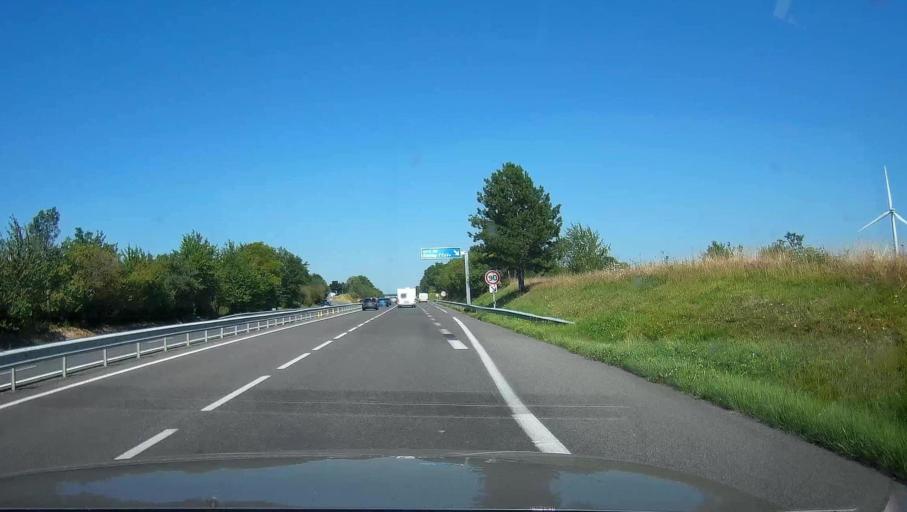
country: FR
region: Champagne-Ardenne
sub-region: Departement de l'Aube
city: Mailly-le-Camp
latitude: 48.6317
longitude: 4.1808
